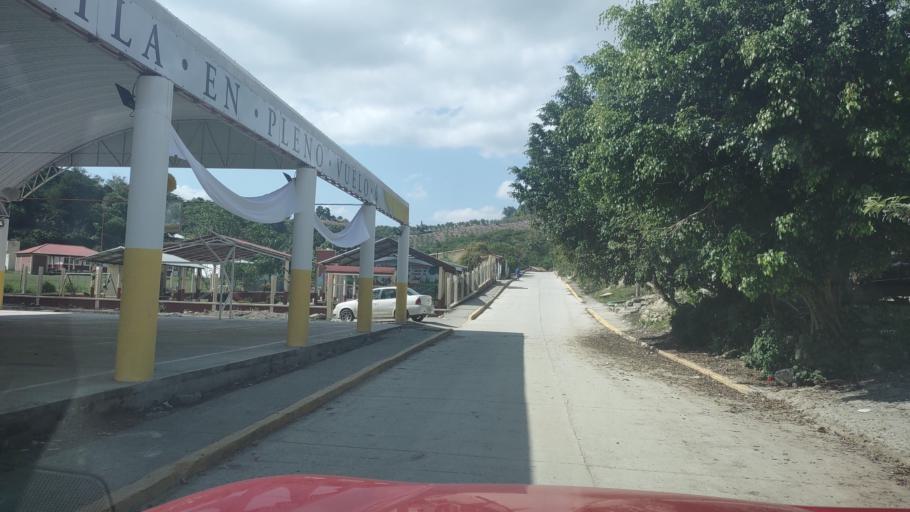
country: MX
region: Veracruz
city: Agua Dulce
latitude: 20.2950
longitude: -97.1496
